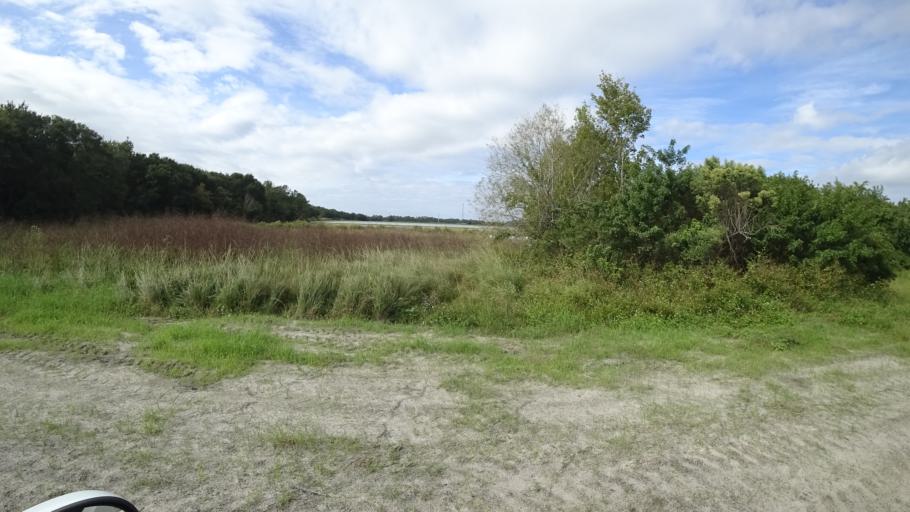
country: US
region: Florida
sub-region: Hillsborough County
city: Wimauma
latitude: 27.5980
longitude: -82.3243
